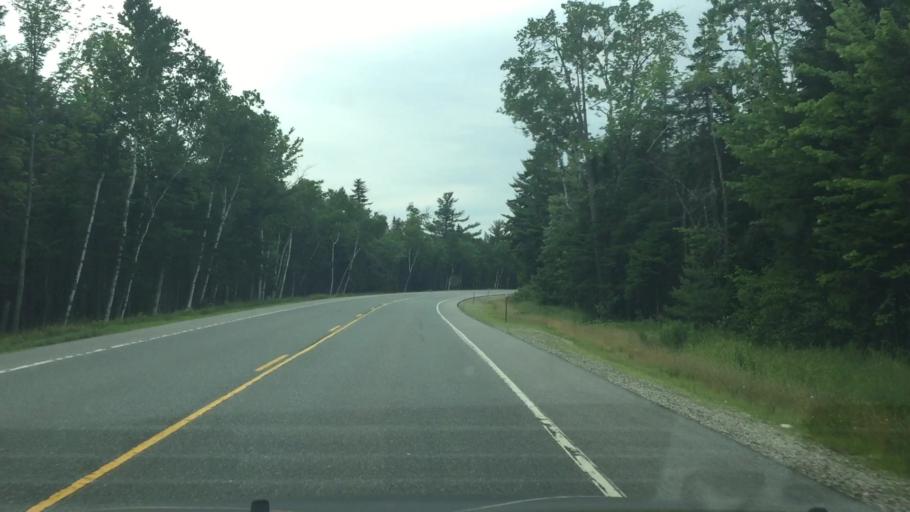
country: US
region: New Hampshire
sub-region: Grafton County
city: Deerfield
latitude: 44.2249
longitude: -71.6743
